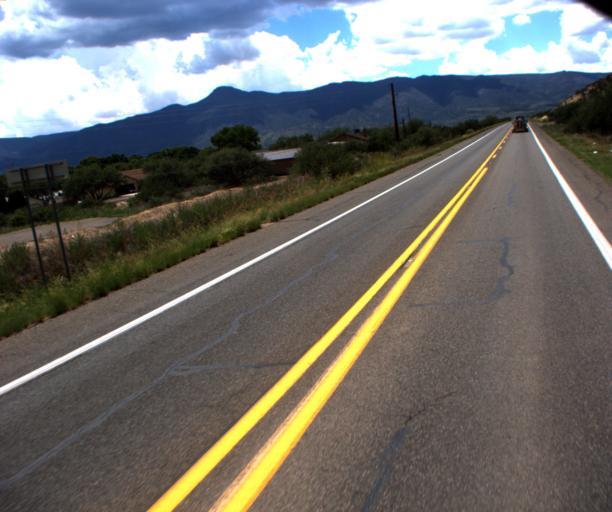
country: US
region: Arizona
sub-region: Yavapai County
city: Camp Verde
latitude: 34.5287
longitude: -111.7952
